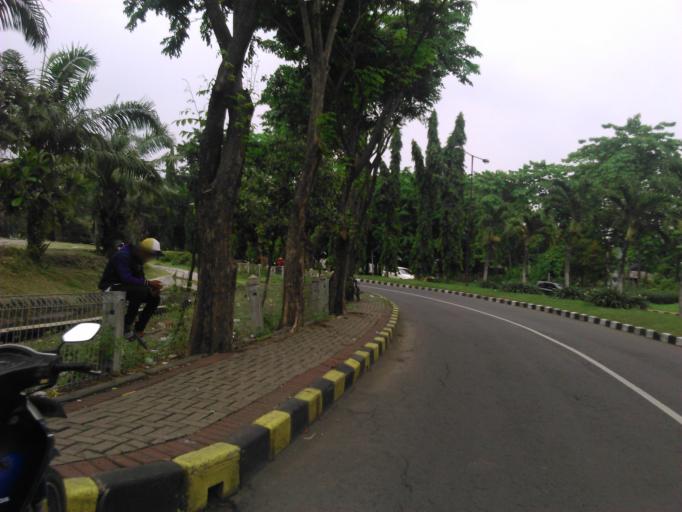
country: ID
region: East Java
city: Mulyorejo
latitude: -7.2764
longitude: 112.7905
